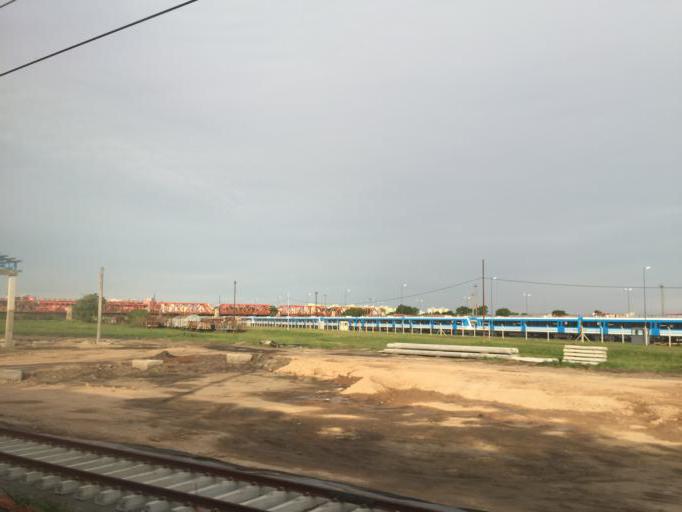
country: AR
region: Buenos Aires
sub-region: Partido de Avellaneda
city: Avellaneda
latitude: -34.6757
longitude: -58.3789
